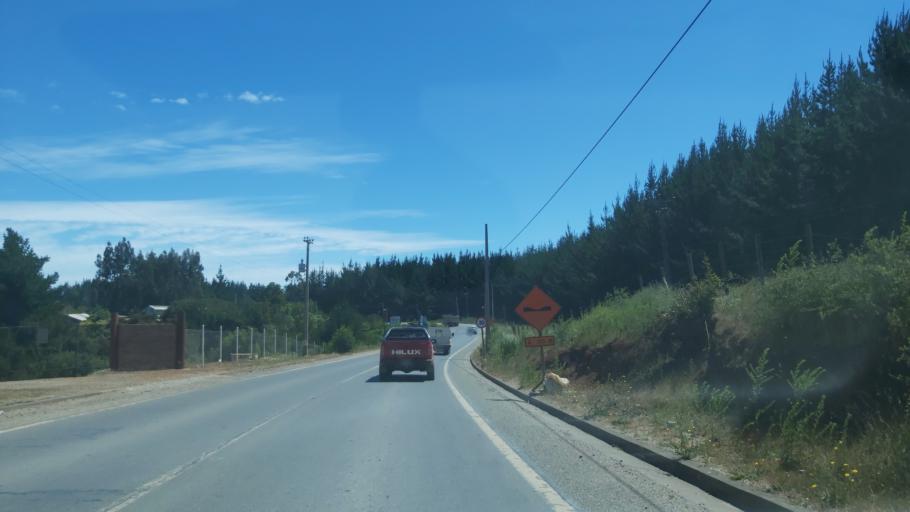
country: CL
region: Maule
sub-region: Provincia de Talca
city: Constitucion
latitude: -35.3981
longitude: -72.4336
